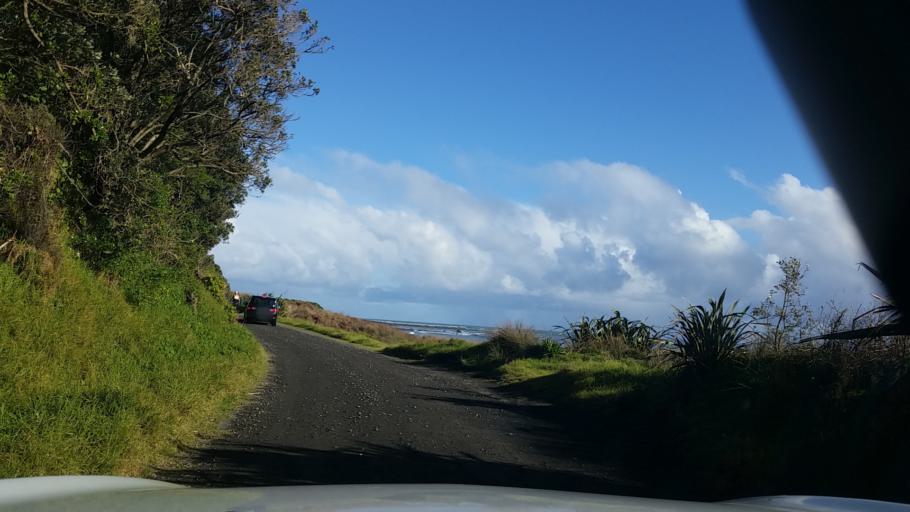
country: NZ
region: Taranaki
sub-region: New Plymouth District
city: New Plymouth
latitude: -39.1176
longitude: 173.9300
